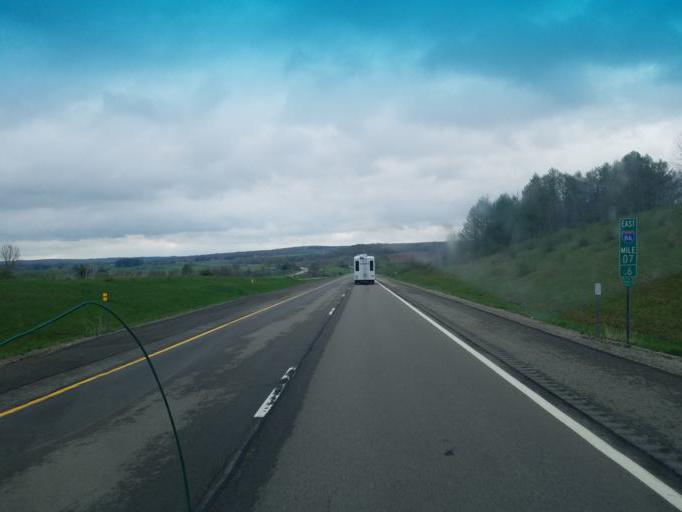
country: US
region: New York
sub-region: Chautauqua County
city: Clymer
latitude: 42.1461
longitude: -79.6208
